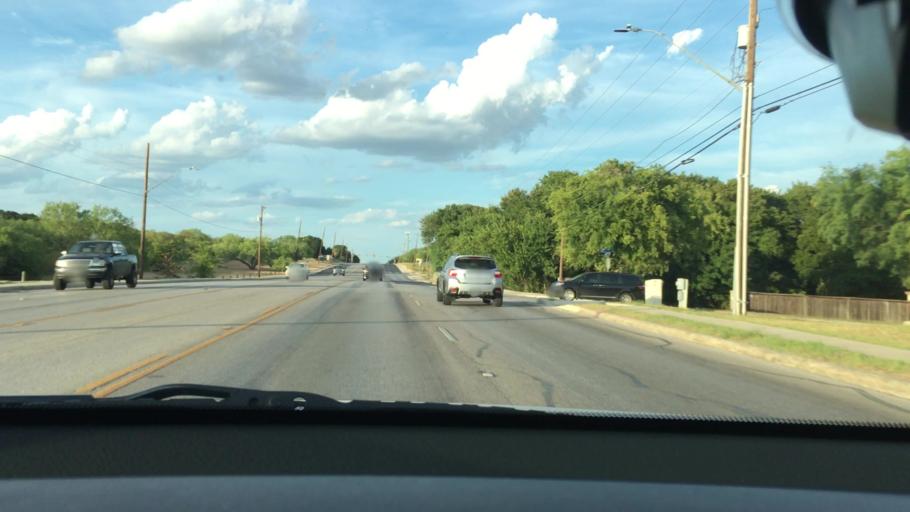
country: US
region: Texas
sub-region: Bexar County
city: Live Oak
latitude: 29.5805
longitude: -98.3695
